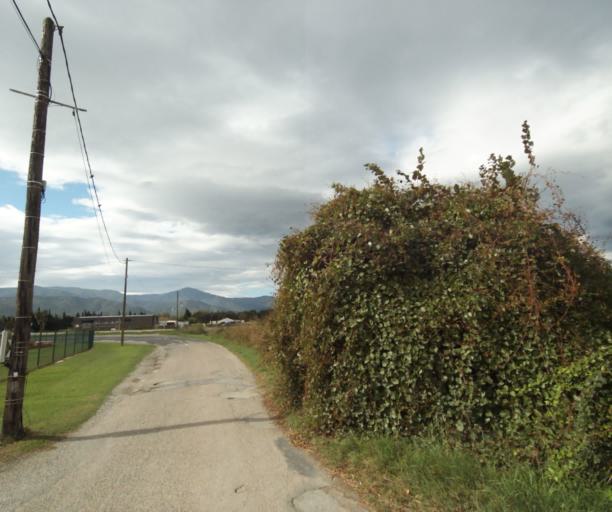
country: FR
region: Languedoc-Roussillon
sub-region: Departement des Pyrenees-Orientales
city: Argelers
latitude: 42.5773
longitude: 3.0348
